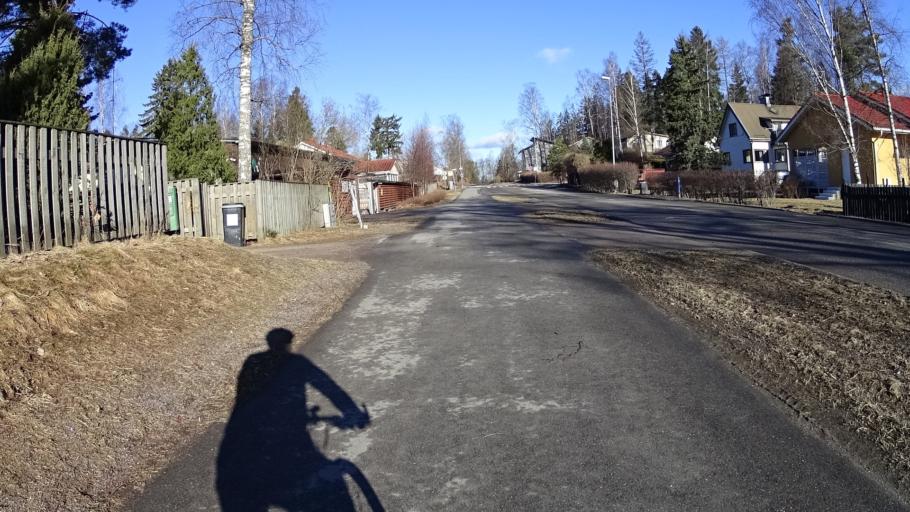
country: FI
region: Uusimaa
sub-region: Helsinki
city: Kilo
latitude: 60.2541
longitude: 24.7718
